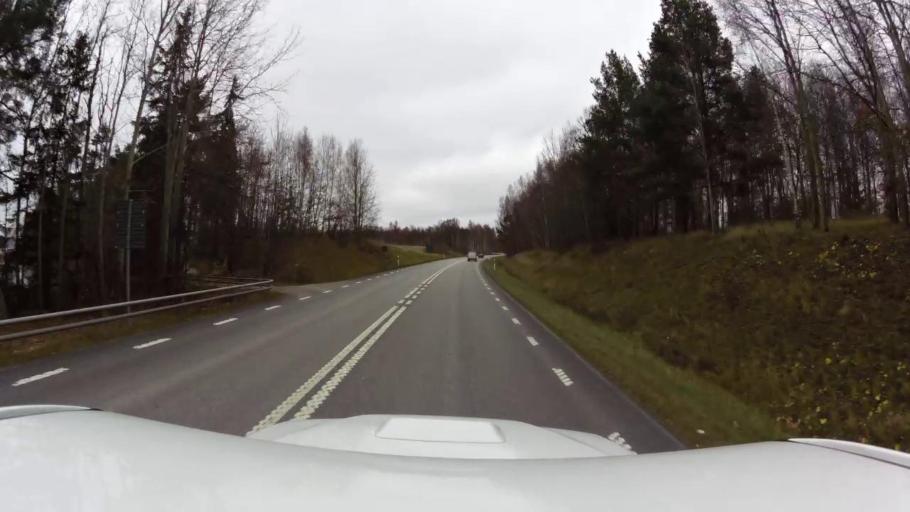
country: SE
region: OEstergoetland
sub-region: Kinda Kommun
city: Rimforsa
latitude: 58.1561
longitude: 15.6799
